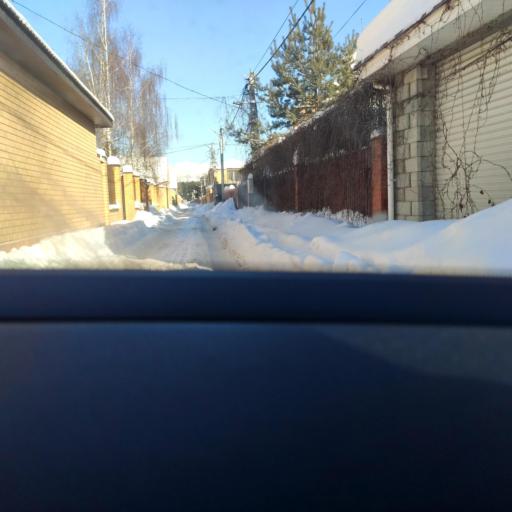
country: RU
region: Moskovskaya
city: Mosrentgen
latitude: 55.6281
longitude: 37.4614
